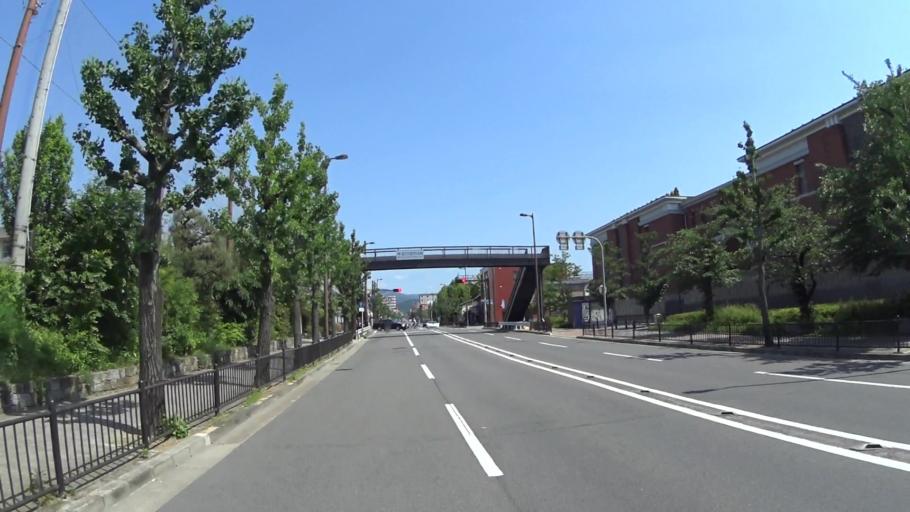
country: JP
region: Kyoto
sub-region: Kyoto-shi
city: Kamigyo-ku
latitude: 35.0329
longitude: 135.7594
